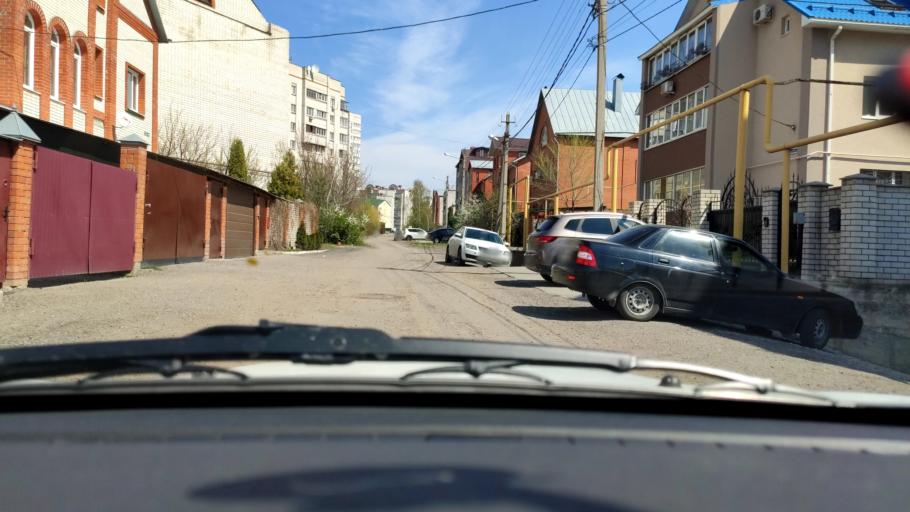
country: RU
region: Voronezj
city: Podgornoye
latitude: 51.7205
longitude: 39.1536
